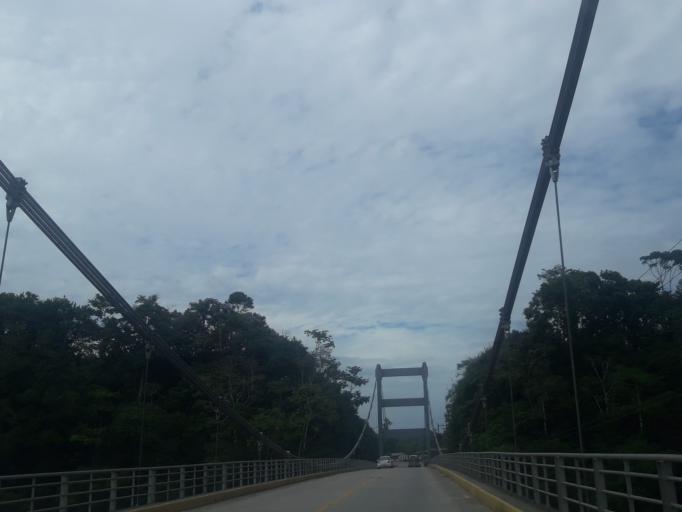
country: EC
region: Napo
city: Tena
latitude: -1.0441
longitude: -77.7967
